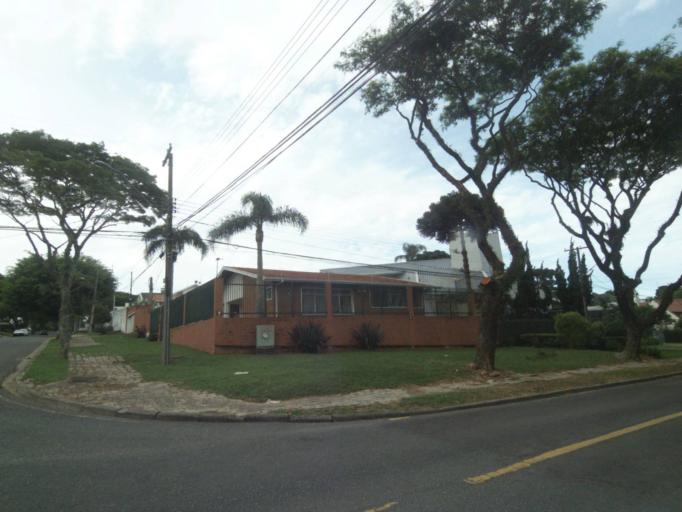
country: BR
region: Parana
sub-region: Curitiba
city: Curitiba
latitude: -25.4263
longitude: -49.2369
